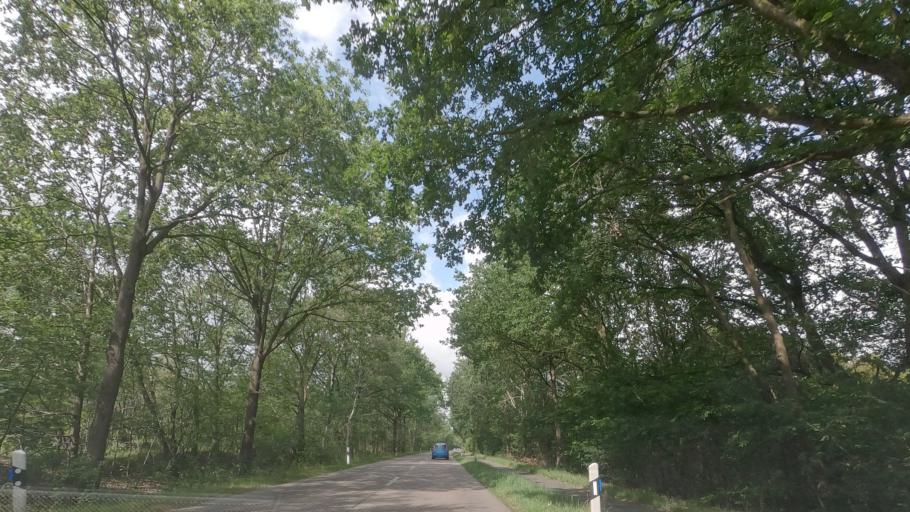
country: DE
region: Lower Saxony
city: Schwanewede
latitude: 53.2311
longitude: 8.5643
